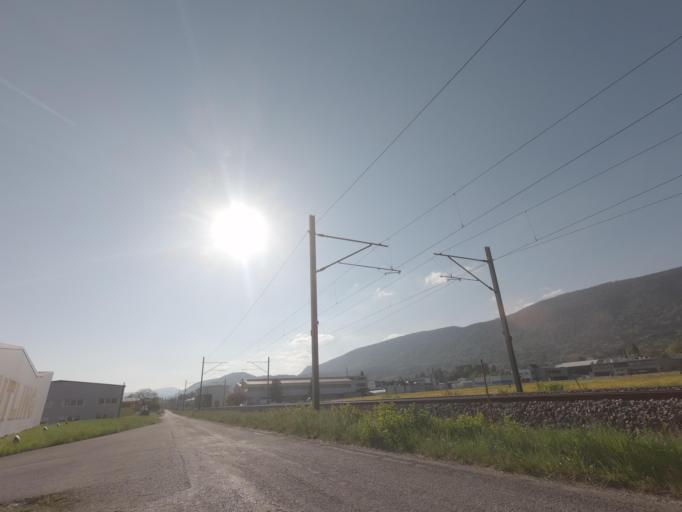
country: CH
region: Solothurn
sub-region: Bezirk Lebern
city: Bettlach
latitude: 47.1915
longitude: 7.4127
